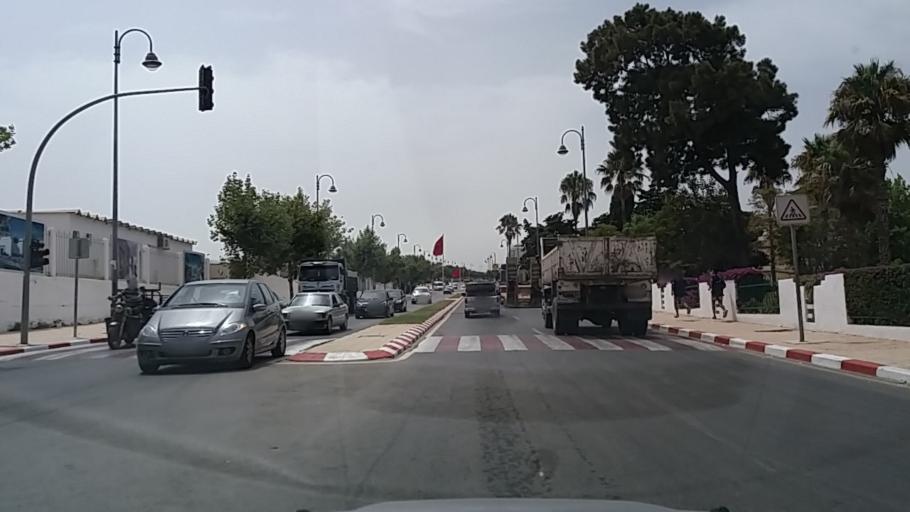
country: MA
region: Tanger-Tetouan
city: Asilah
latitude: 35.4656
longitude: -6.0305
